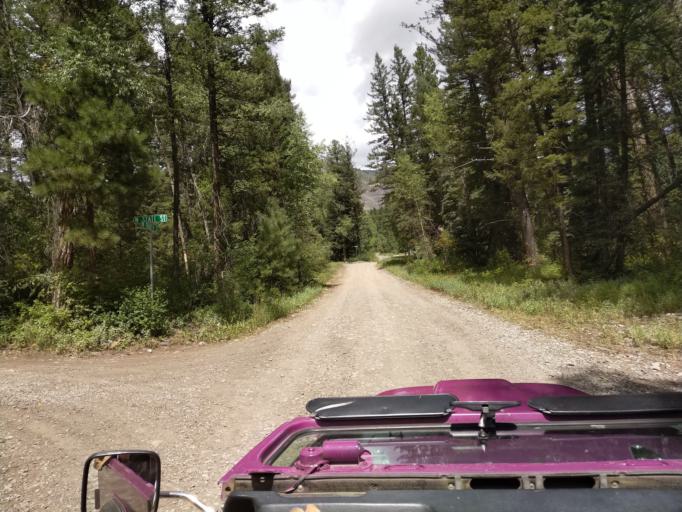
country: US
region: Colorado
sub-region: Gunnison County
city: Crested Butte
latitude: 39.0710
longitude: -107.1919
